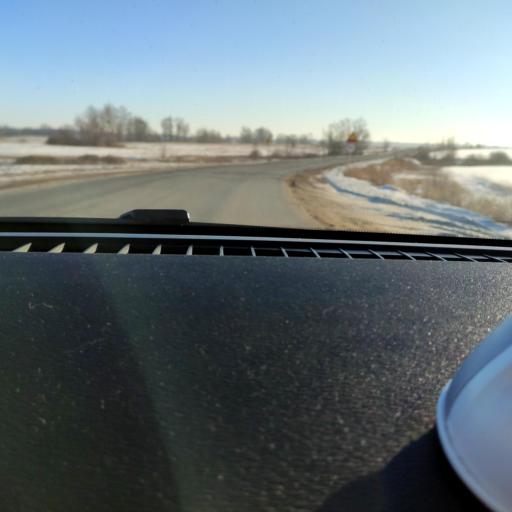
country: RU
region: Samara
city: Spiridonovka
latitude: 53.1353
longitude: 50.6072
